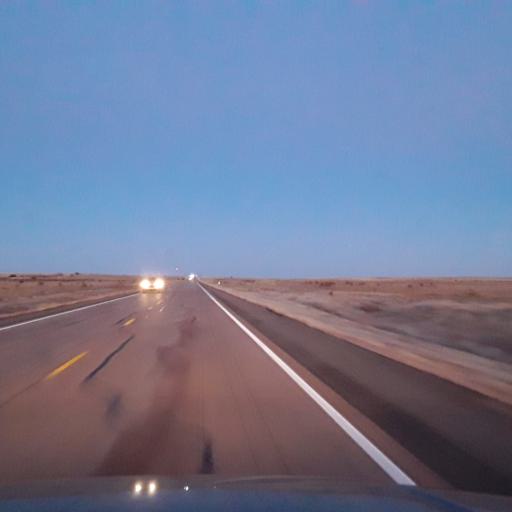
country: US
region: New Mexico
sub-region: Guadalupe County
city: Santa Rosa
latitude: 34.7618
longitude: -104.9861
